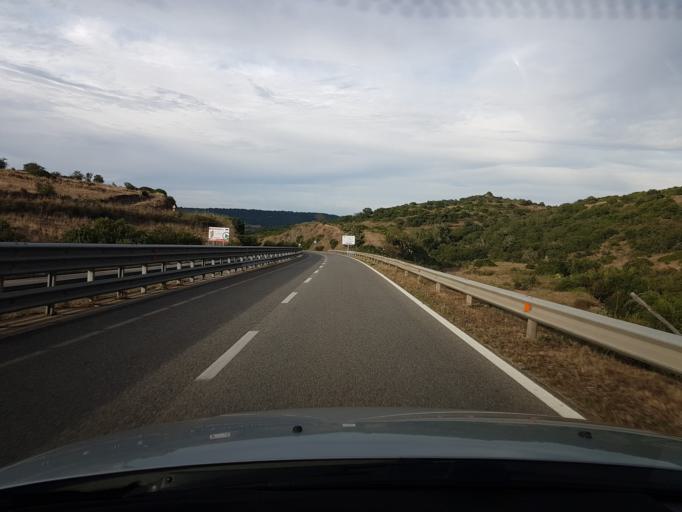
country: IT
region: Sardinia
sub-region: Provincia di Oristano
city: Soddi
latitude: 40.1336
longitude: 8.8661
